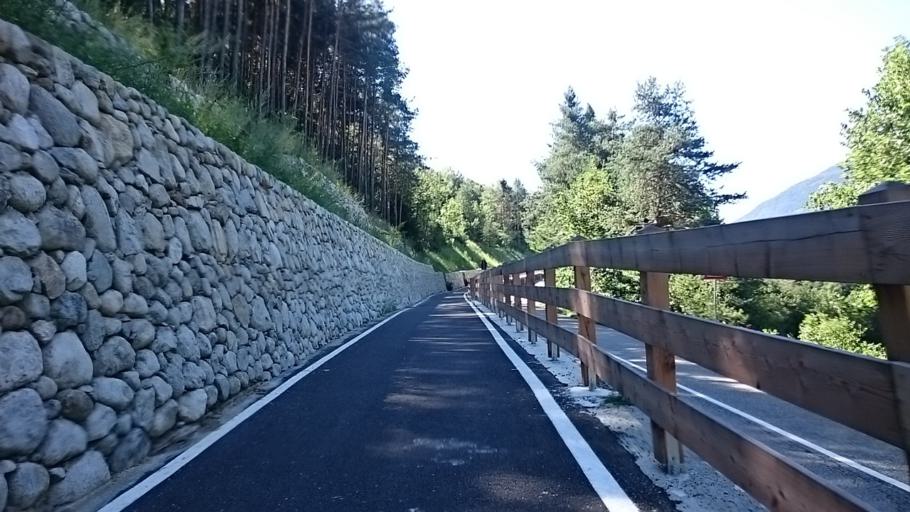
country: IT
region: Trentino-Alto Adige
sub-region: Bolzano
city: Naz-Sciaves - Natz-Schabs
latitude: 46.7716
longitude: 11.6467
